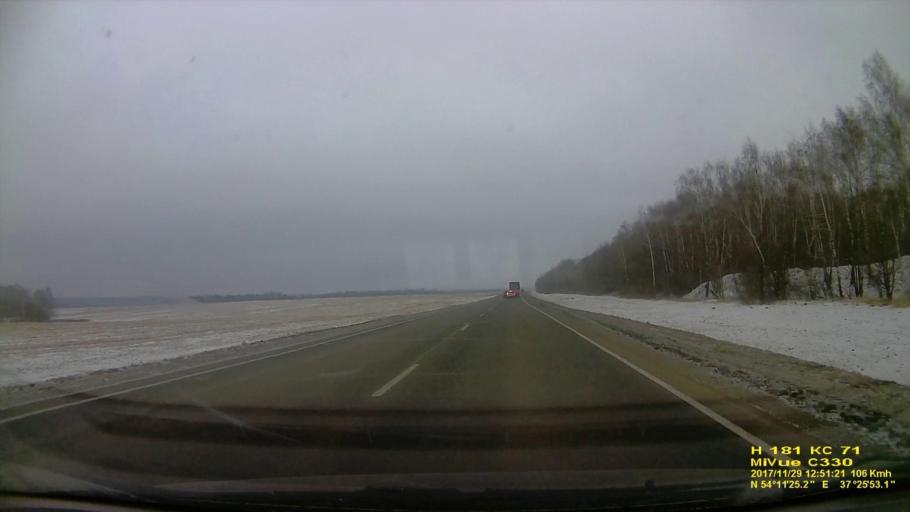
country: RU
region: Tula
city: Barsuki
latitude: 54.1904
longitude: 37.4313
